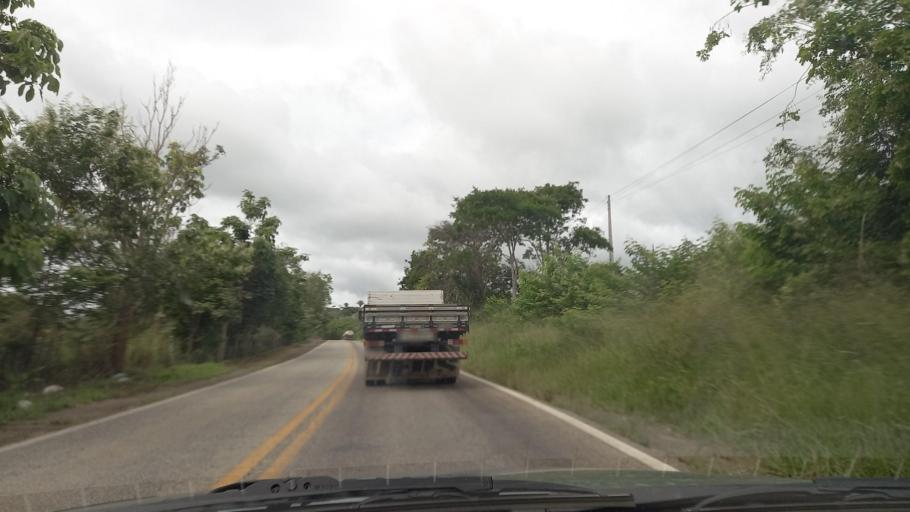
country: BR
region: Pernambuco
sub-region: Canhotinho
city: Canhotinho
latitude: -8.8654
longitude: -36.1856
